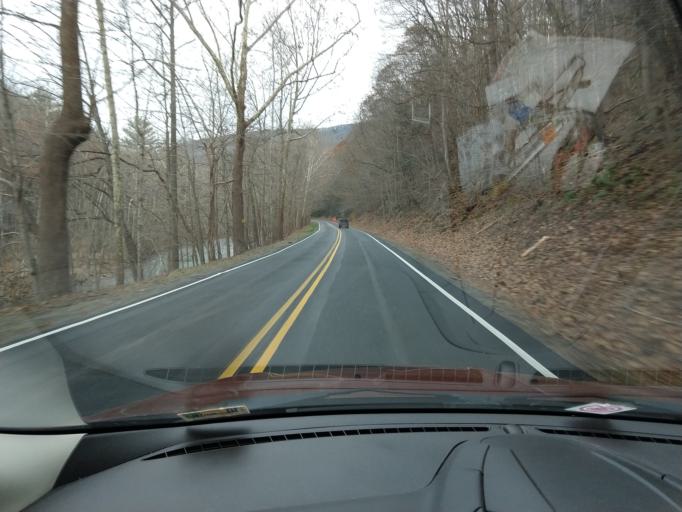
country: US
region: Virginia
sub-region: City of Covington
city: Covington
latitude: 37.7562
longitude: -80.1363
